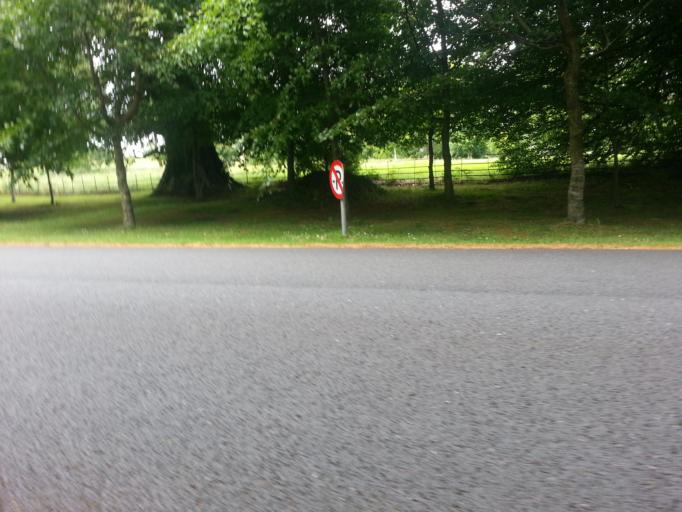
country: IE
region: Leinster
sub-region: Wicklow
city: Enniskerry
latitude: 53.1861
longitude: -6.1791
